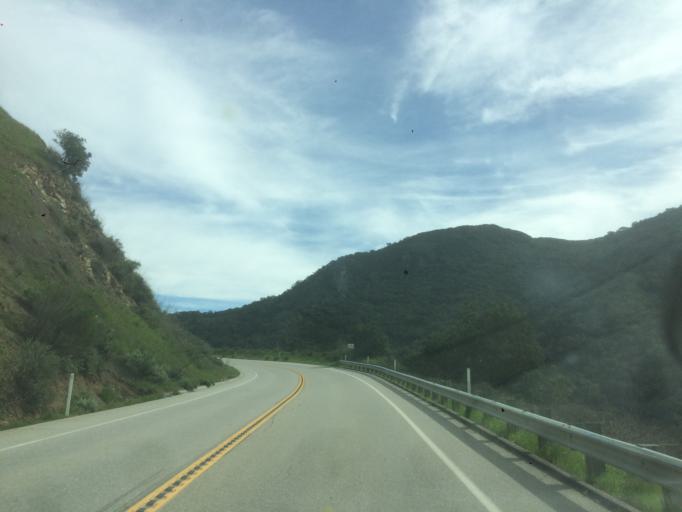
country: US
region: California
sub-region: San Luis Obispo County
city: Arroyo Grande
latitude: 35.1875
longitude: -120.4937
